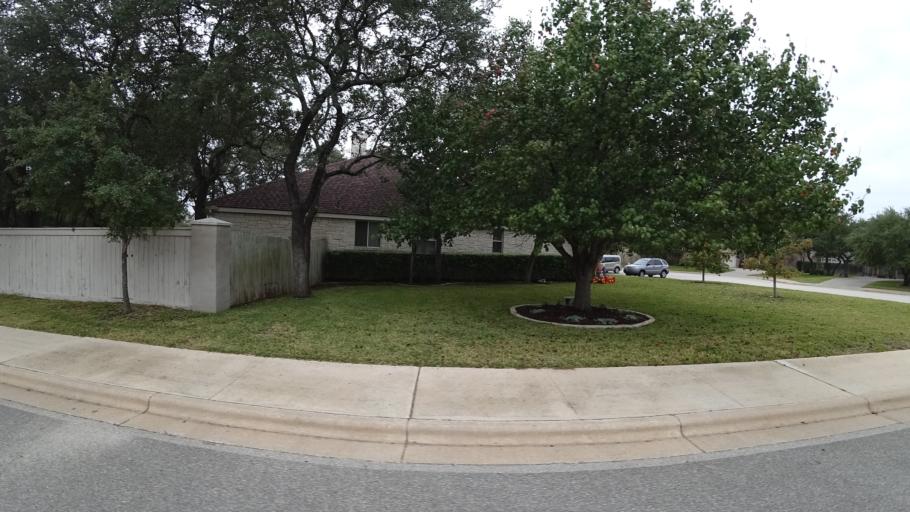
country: US
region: Texas
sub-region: Travis County
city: Bee Cave
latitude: 30.3099
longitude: -97.9322
